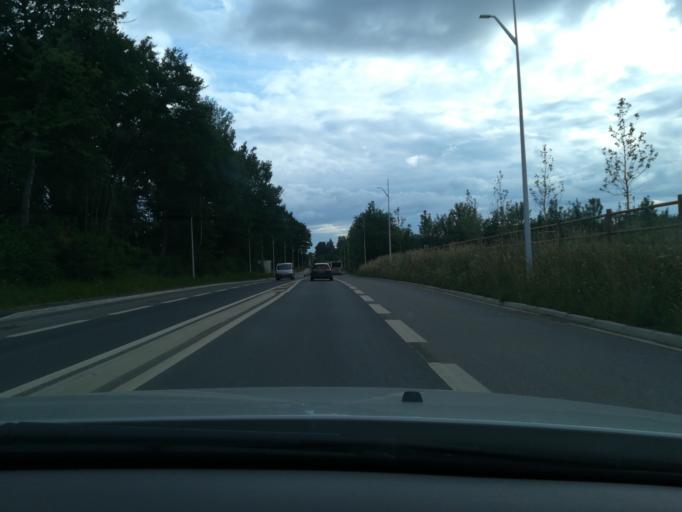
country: FR
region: Haute-Normandie
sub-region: Departement de la Seine-Maritime
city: Isneauville
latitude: 49.4860
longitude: 1.1372
